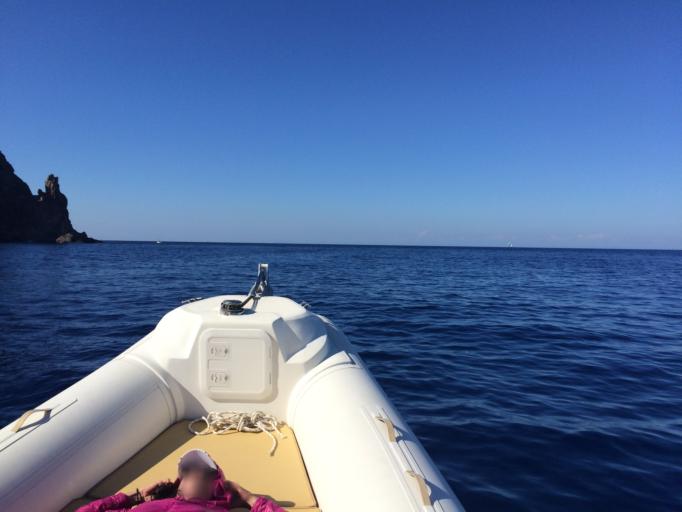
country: IT
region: Tuscany
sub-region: Provincia di Livorno
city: Capraia Isola
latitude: 43.0417
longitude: 9.8491
